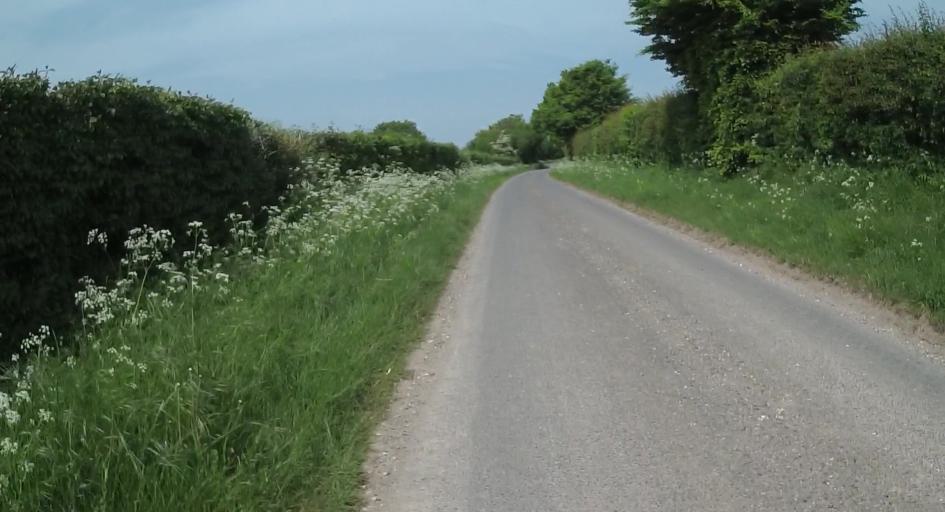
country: GB
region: England
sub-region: Hampshire
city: Overton
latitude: 51.2762
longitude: -1.2325
